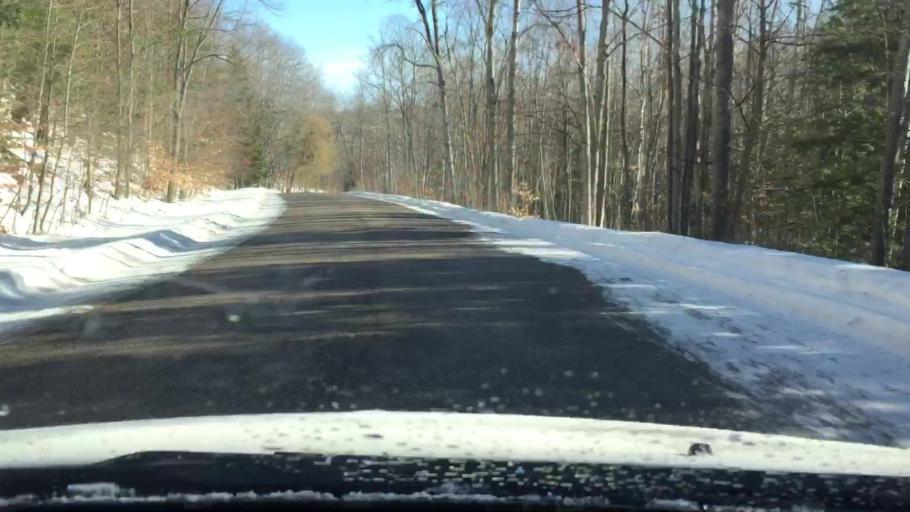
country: US
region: Michigan
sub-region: Charlevoix County
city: East Jordan
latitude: 45.1032
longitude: -85.1441
